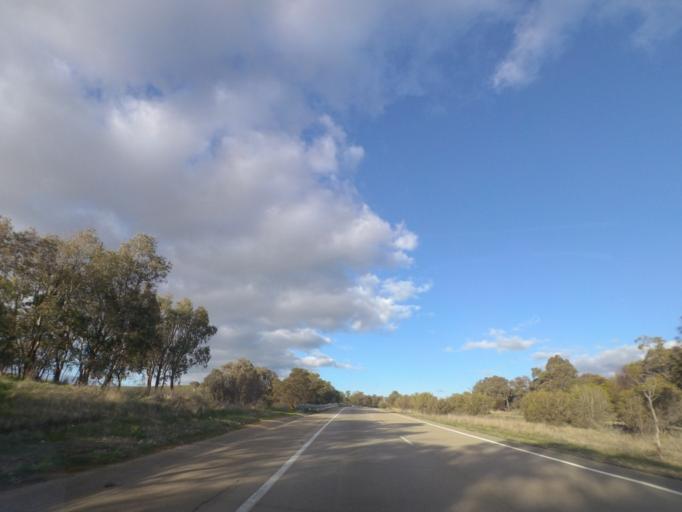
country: AU
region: New South Wales
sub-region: Yass Valley
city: Yass
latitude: -34.8029
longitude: 148.5536
